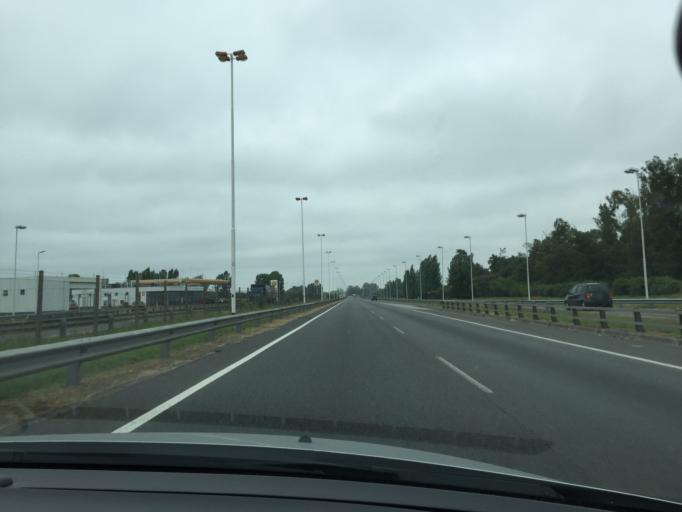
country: AR
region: Buenos Aires
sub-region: Partido de Ezeiza
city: Ezeiza
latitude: -34.8605
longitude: -58.5644
